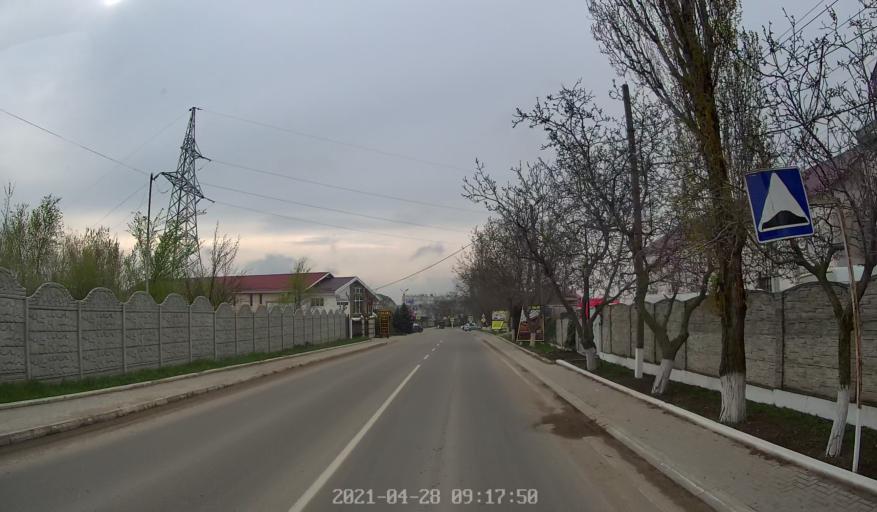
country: MD
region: Chisinau
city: Chisinau
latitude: 46.9853
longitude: 28.9302
